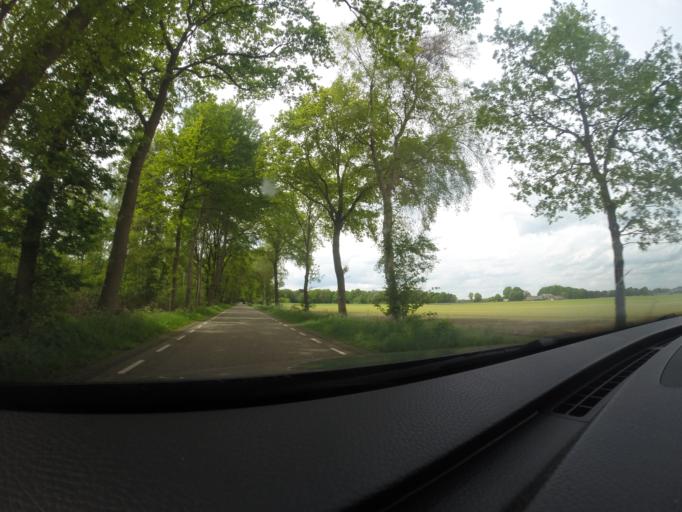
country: NL
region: Overijssel
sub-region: Gemeente Raalte
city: Raalte
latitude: 52.3054
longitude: 6.2995
